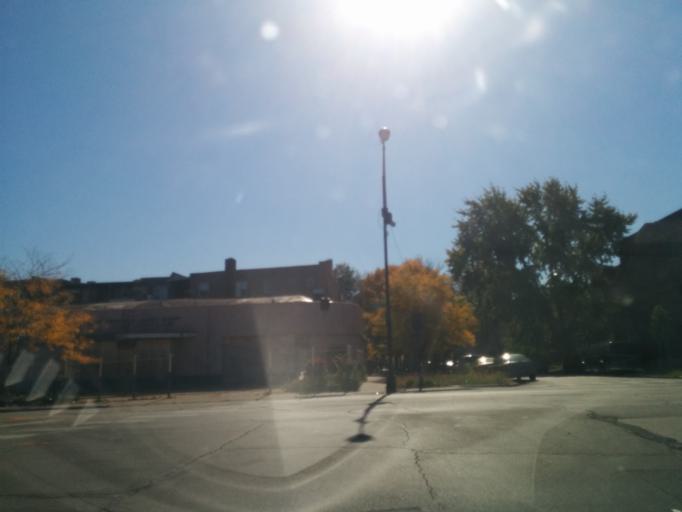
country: US
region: Illinois
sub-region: Cook County
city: Oak Park
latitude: 41.8875
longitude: -87.7632
